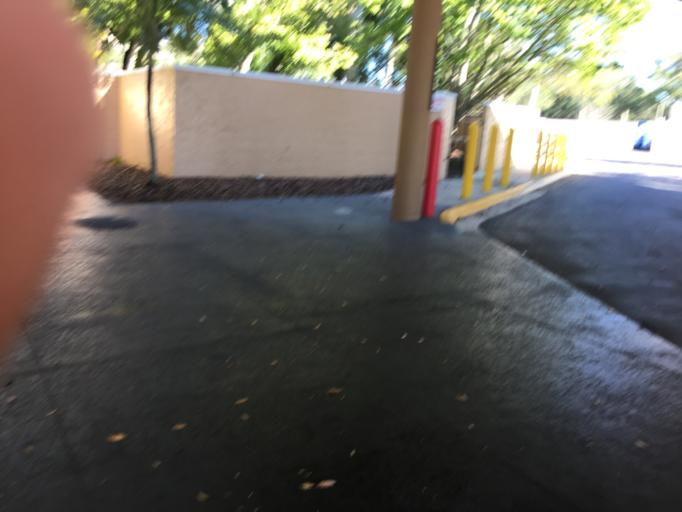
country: US
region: Florida
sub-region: Hillsborough County
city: Egypt Lake-Leto
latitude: 28.0130
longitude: -82.5035
